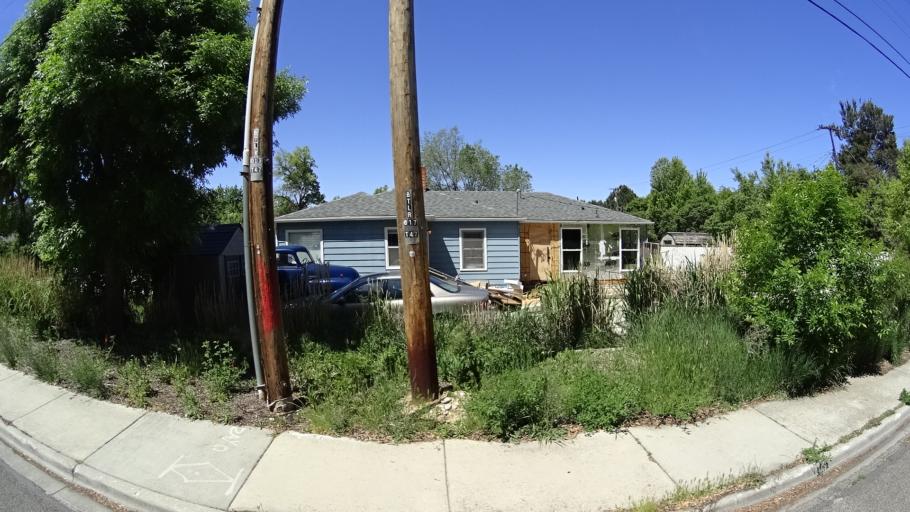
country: US
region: Idaho
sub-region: Ada County
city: Boise
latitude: 43.5792
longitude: -116.1836
